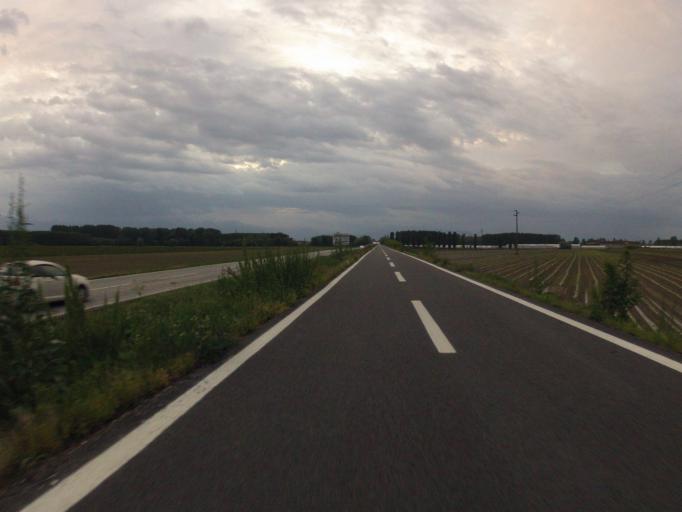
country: IT
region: Piedmont
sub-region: Provincia di Torino
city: Villafranca Piemonte
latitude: 44.7760
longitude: 7.5181
